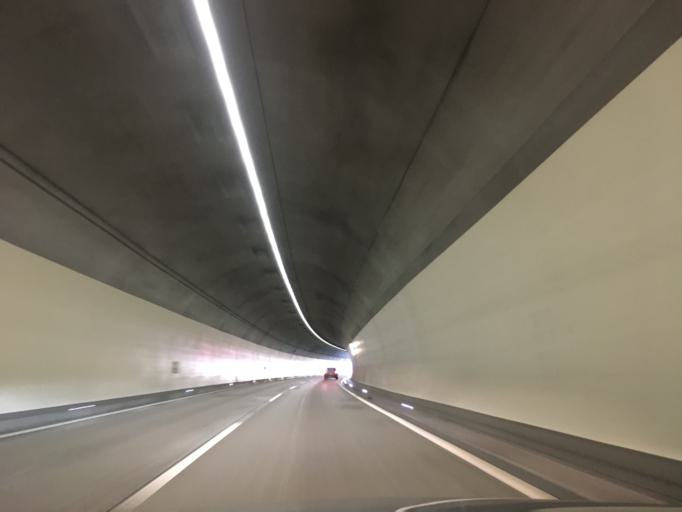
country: CH
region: Saint Gallen
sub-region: Wahlkreis Sarganserland
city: Quarten
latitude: 47.1112
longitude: 9.2568
